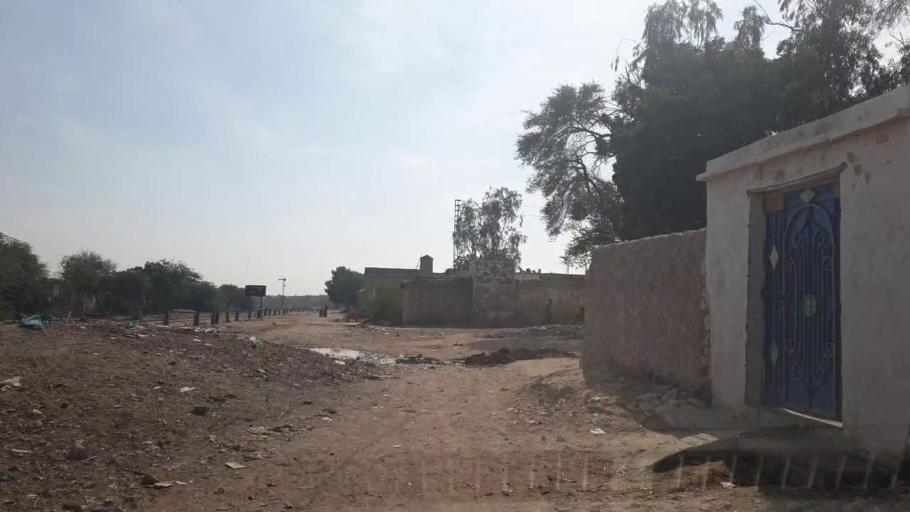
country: PK
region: Sindh
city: Hala
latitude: 25.7451
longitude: 68.2945
